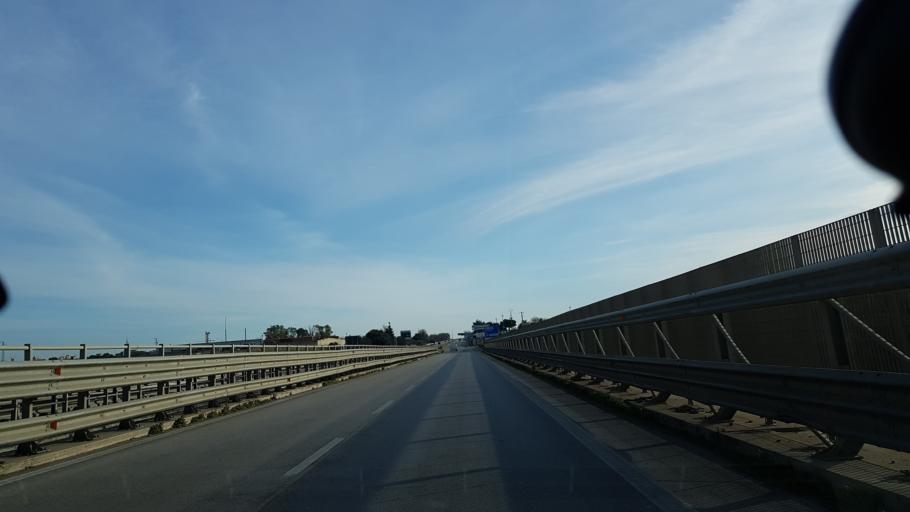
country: IT
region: Apulia
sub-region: Provincia di Brindisi
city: Brindisi
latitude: 40.6384
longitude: 17.9155
